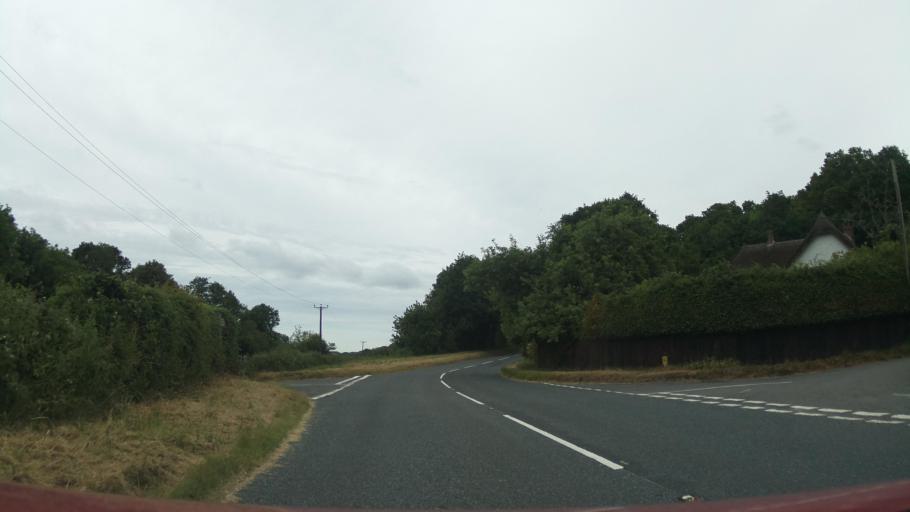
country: GB
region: England
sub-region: Devon
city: Bovey Tracey
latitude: 50.6744
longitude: -3.6511
